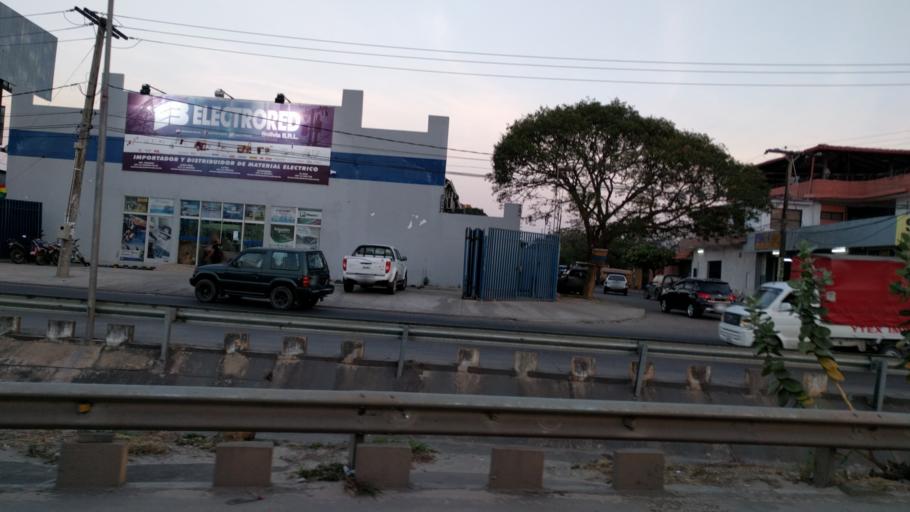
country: BO
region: Santa Cruz
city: Santa Cruz de la Sierra
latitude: -17.7656
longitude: -63.1496
